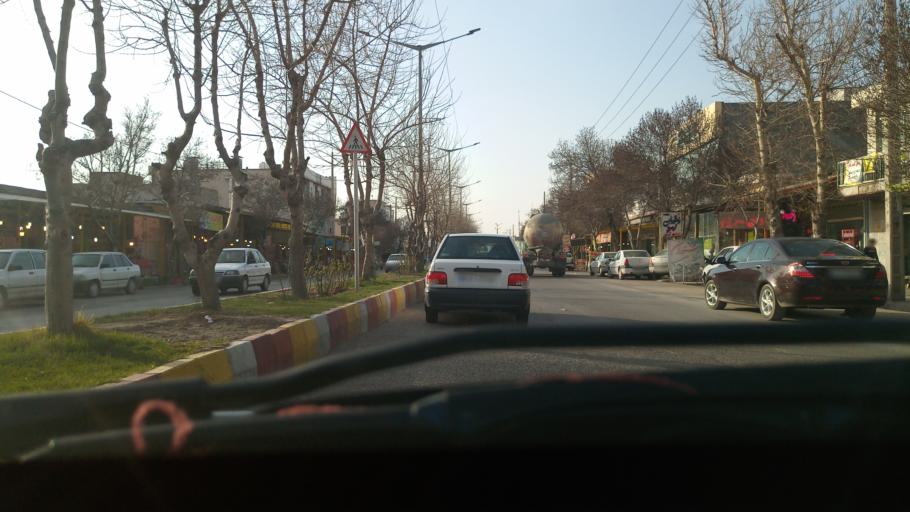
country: IR
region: Khorasan-e Shomali
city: Faruj
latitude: 37.2311
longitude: 58.2209
